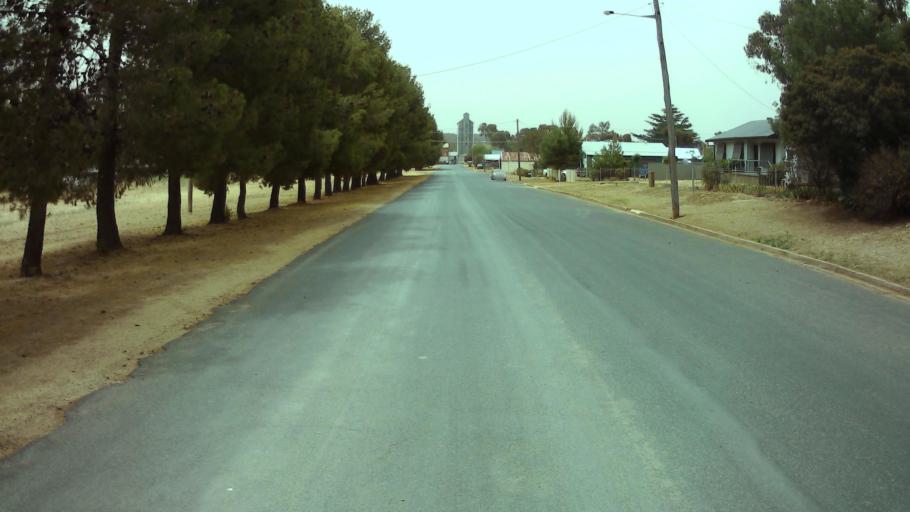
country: AU
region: New South Wales
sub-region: Weddin
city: Grenfell
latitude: -33.8984
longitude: 148.1556
